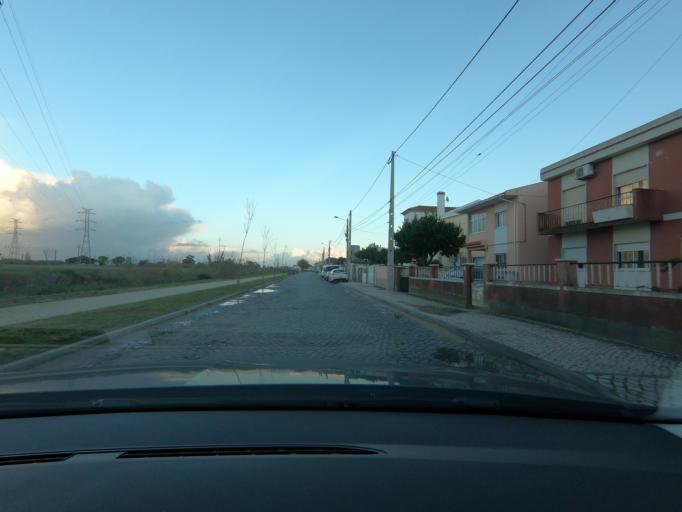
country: PT
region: Lisbon
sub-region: Vila Franca de Xira
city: Castanheira do Ribatejo
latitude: 39.0087
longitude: -8.9561
